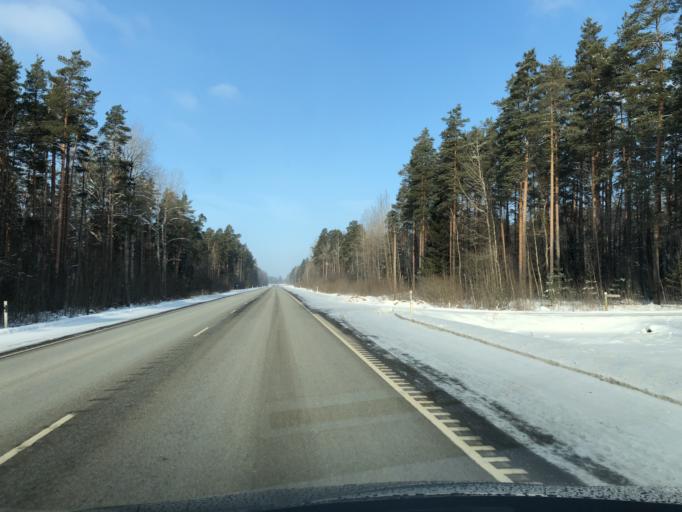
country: EE
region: Tartu
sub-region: Tartu linn
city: Tartu
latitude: 58.3957
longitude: 26.6617
